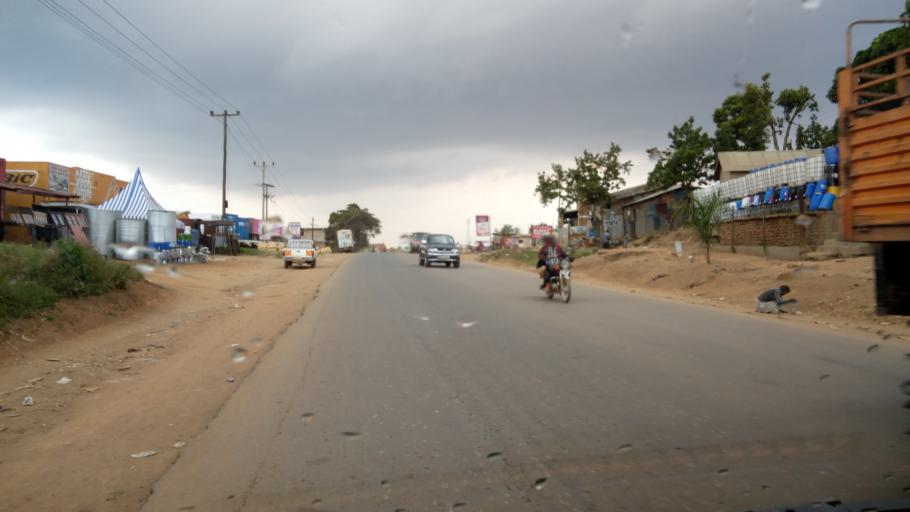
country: UG
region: Central Region
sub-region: Wakiso District
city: Wakiso
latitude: 0.4038
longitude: 32.5440
